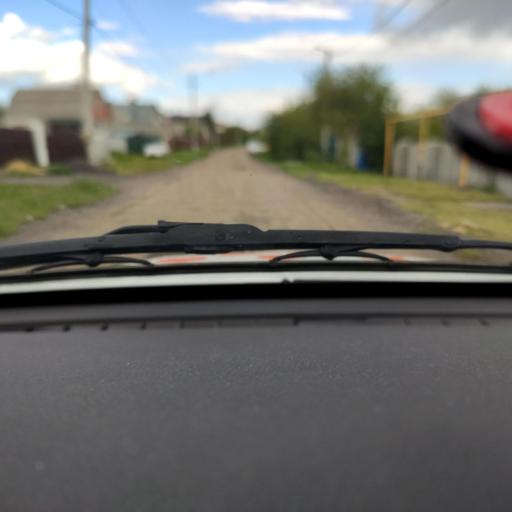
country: RU
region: Voronezj
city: Podgornoye
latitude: 51.7426
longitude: 39.1503
